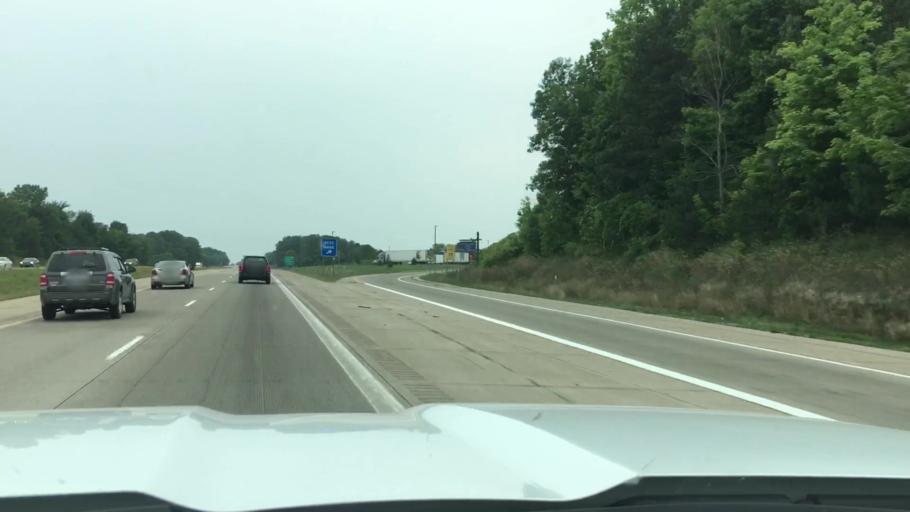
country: US
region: Michigan
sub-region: Ingham County
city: Okemos
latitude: 42.6775
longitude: -84.4023
